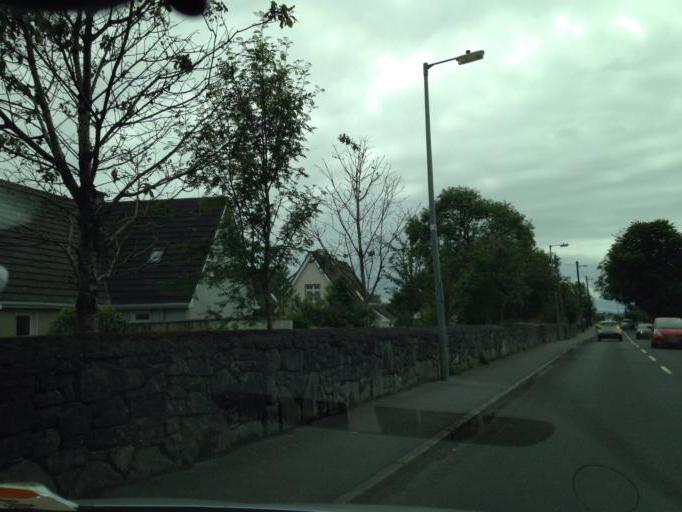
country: IE
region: Connaught
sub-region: County Galway
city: Gaillimh
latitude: 53.2886
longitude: -9.0536
